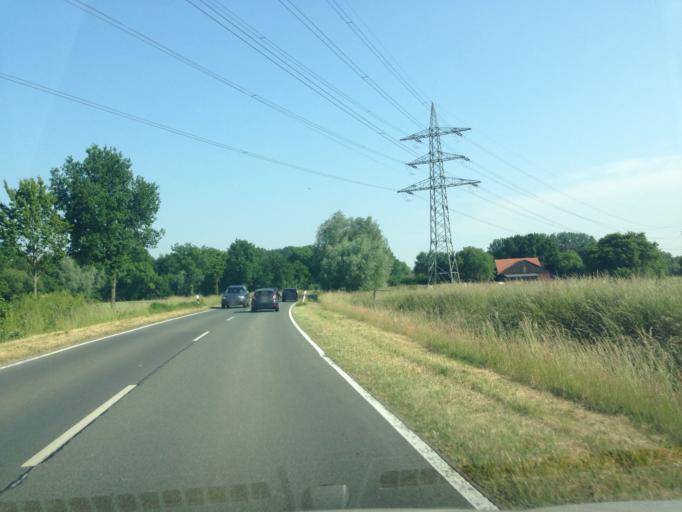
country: DE
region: North Rhine-Westphalia
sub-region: Regierungsbezirk Munster
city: Muenster
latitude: 51.9860
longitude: 7.5473
